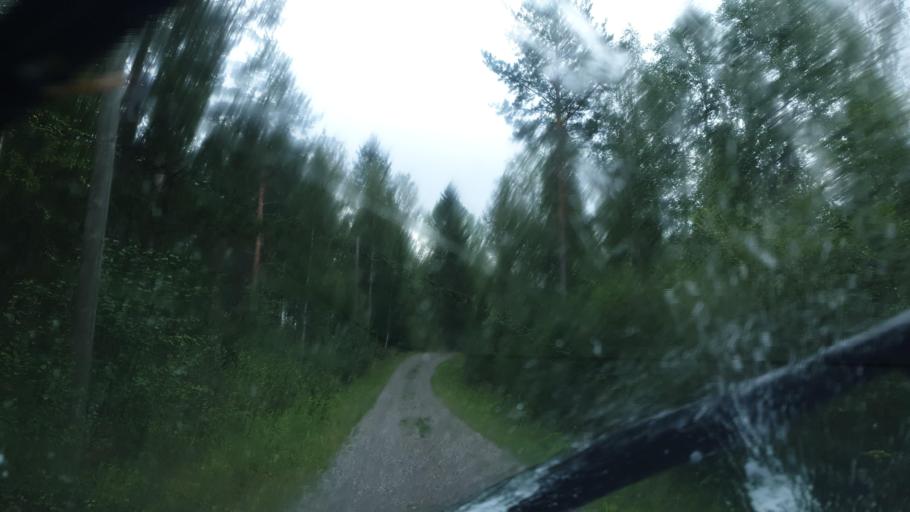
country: FI
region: Northern Savo
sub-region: Kuopio
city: Nilsiae
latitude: 63.2492
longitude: 28.2453
